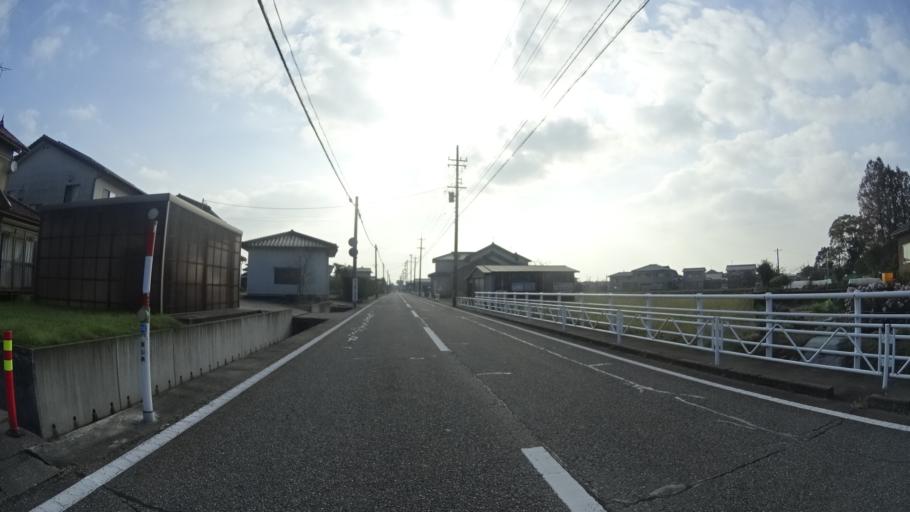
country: JP
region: Toyama
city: Himi
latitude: 36.8747
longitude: 136.9778
